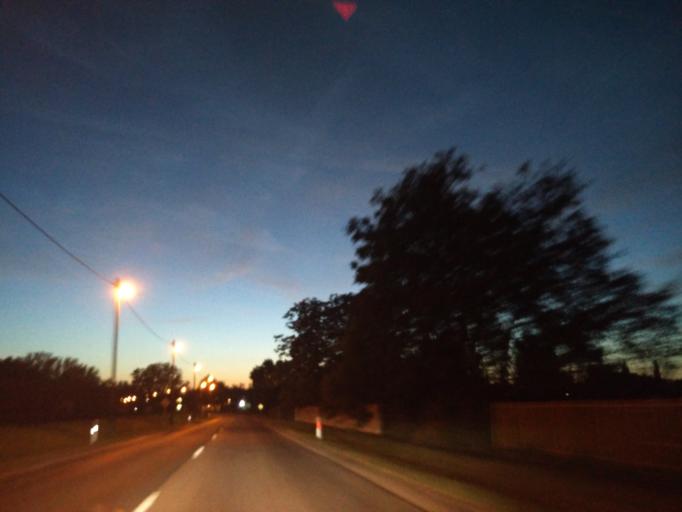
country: HU
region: Vas
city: Vasvar
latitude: 47.0524
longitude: 16.7944
